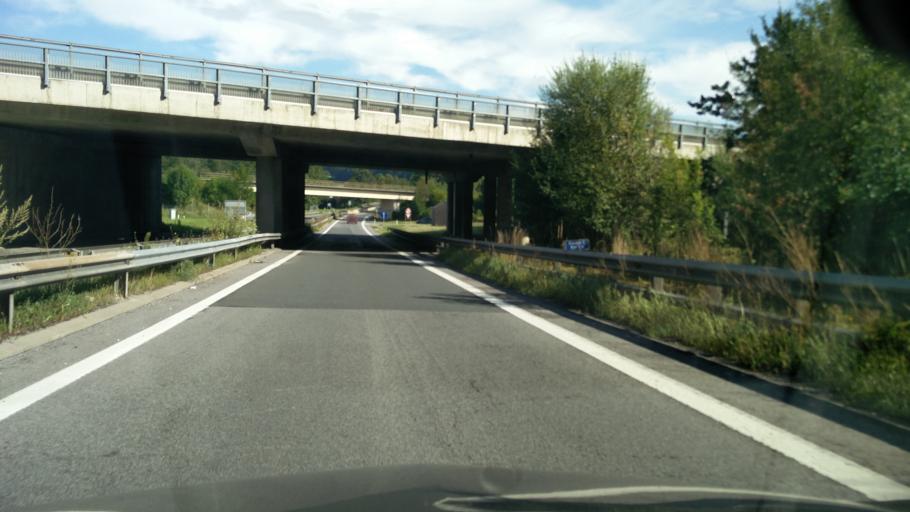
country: AT
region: Styria
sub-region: Politischer Bezirk Weiz
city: Gleisdorf
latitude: 47.0982
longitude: 15.6890
